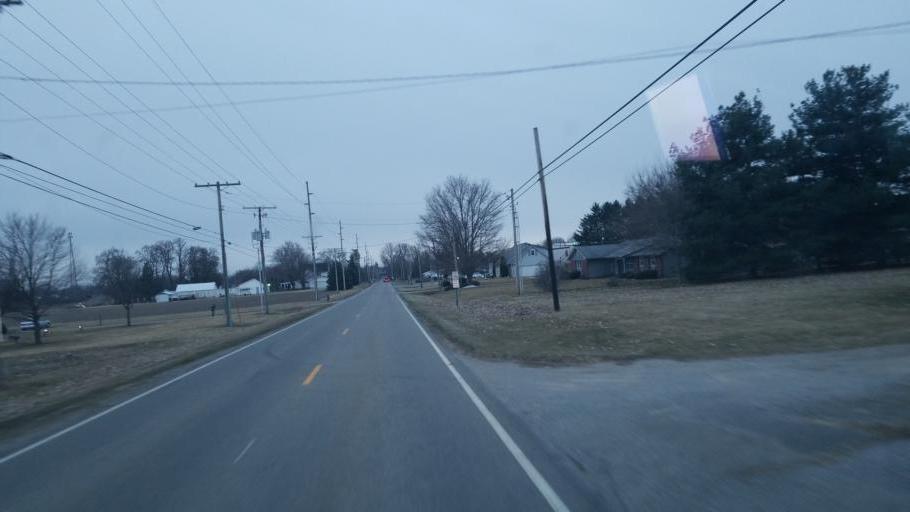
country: US
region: Ohio
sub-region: Defiance County
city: Hicksville
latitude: 41.3060
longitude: -84.7667
